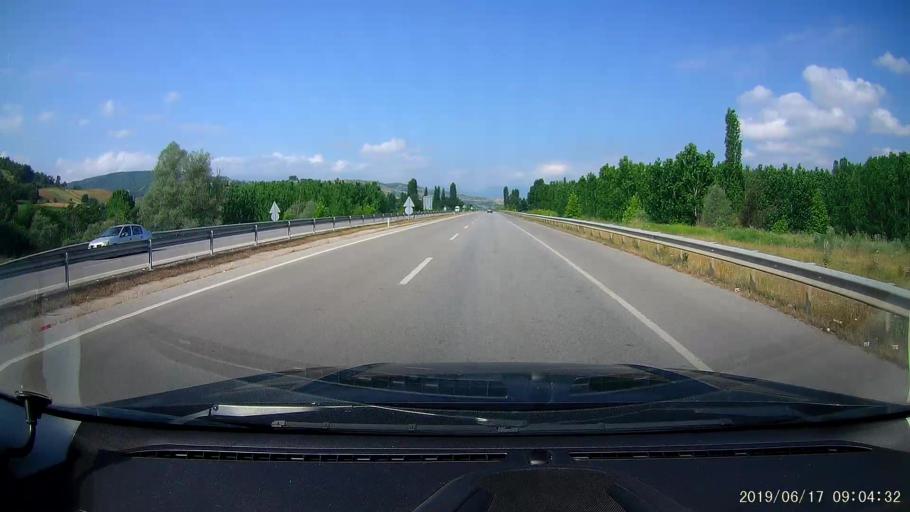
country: TR
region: Amasya
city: Tasova
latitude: 40.7447
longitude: 36.2861
